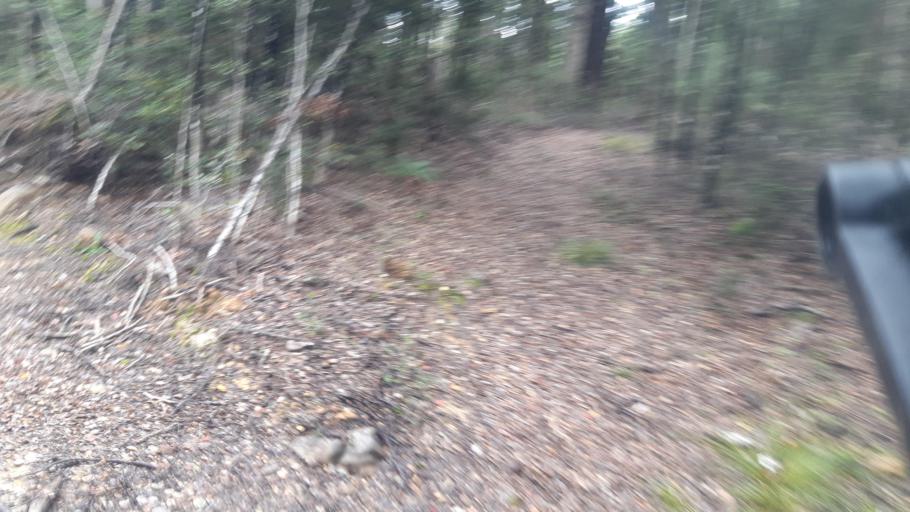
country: NZ
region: Tasman
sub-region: Tasman District
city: Wakefield
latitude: -41.7674
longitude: 172.8159
